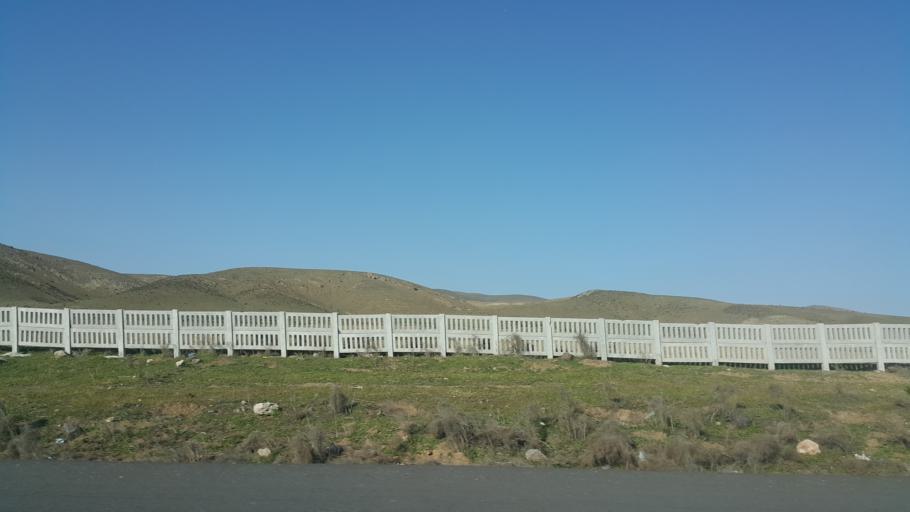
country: TR
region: Aksaray
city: Acipinar
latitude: 38.6986
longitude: 33.6858
